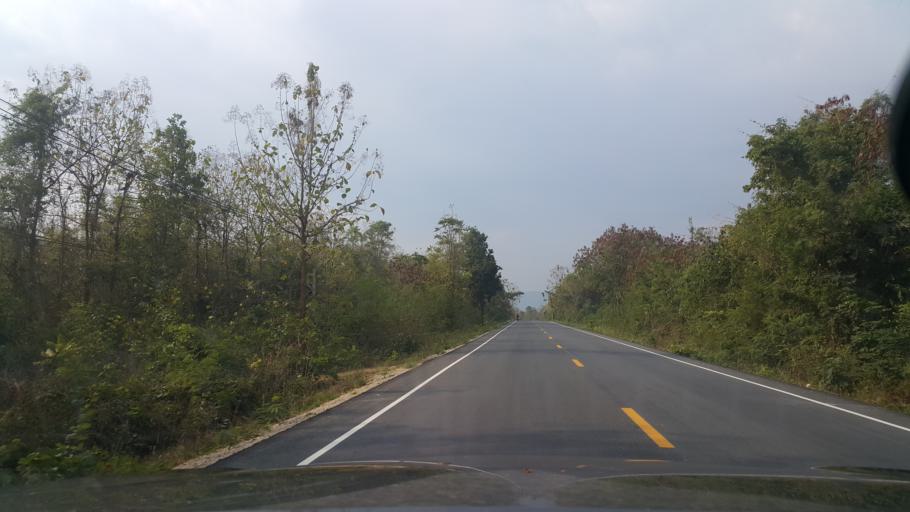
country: TH
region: Sukhothai
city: Thung Saliam
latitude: 17.2547
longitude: 99.5224
